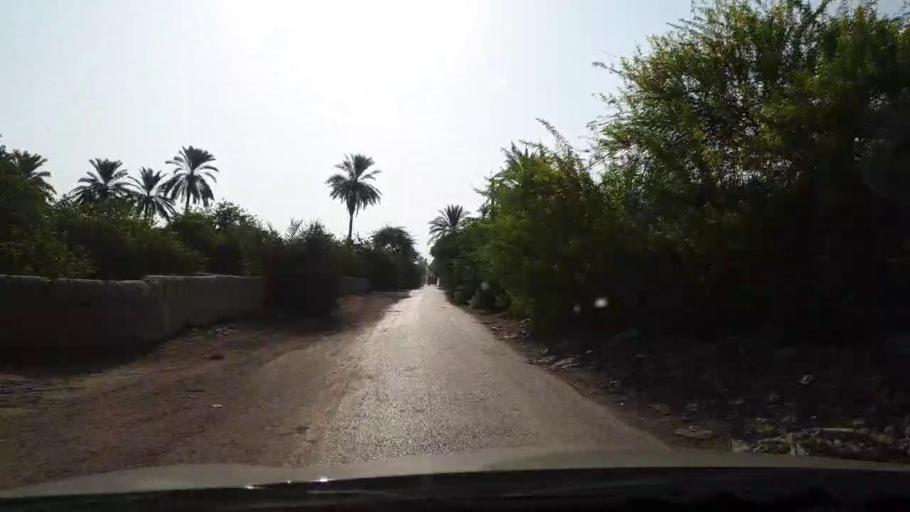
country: PK
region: Sindh
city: Larkana
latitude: 27.5508
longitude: 68.2370
